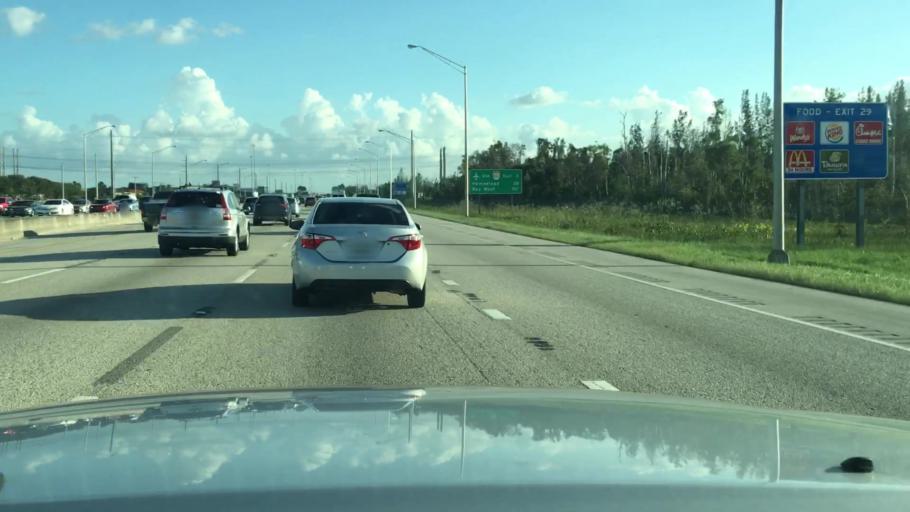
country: US
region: Florida
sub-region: Miami-Dade County
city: Doral
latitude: 25.8227
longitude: -80.3872
